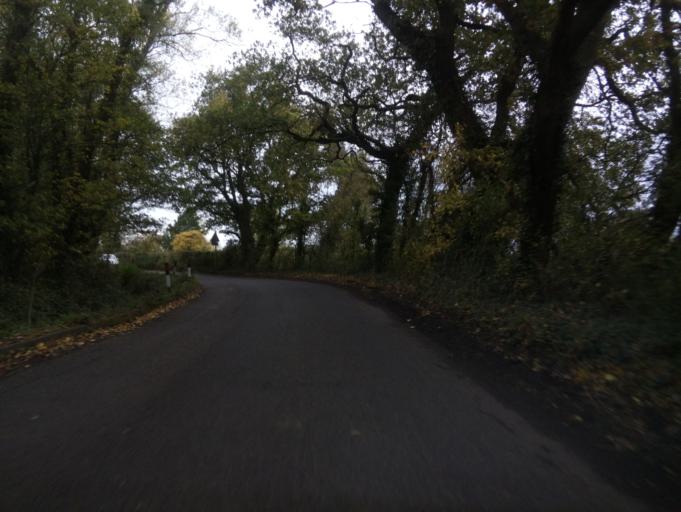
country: GB
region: England
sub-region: Somerset
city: Yeovil
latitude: 51.0075
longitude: -2.5955
